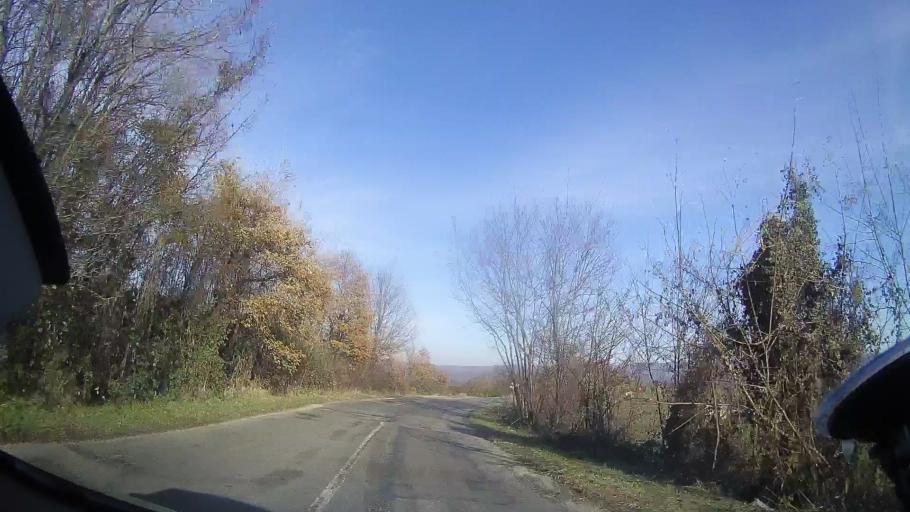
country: RO
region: Bihor
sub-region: Comuna Brusturi
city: Brusturi
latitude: 47.1078
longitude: 22.2555
